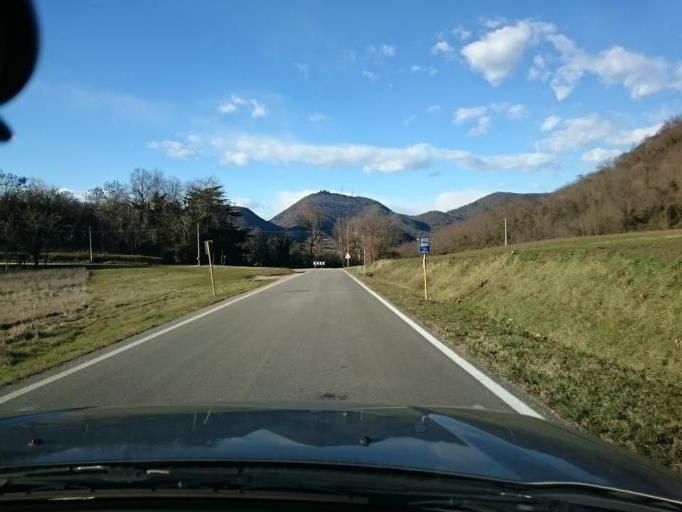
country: IT
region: Veneto
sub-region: Provincia di Padova
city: Vo
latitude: 45.3358
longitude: 11.6816
